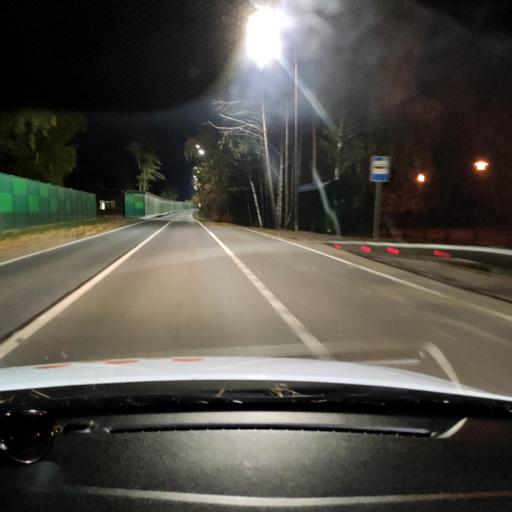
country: RU
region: Tatarstan
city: Verkhniy Uslon
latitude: 55.6258
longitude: 49.0139
